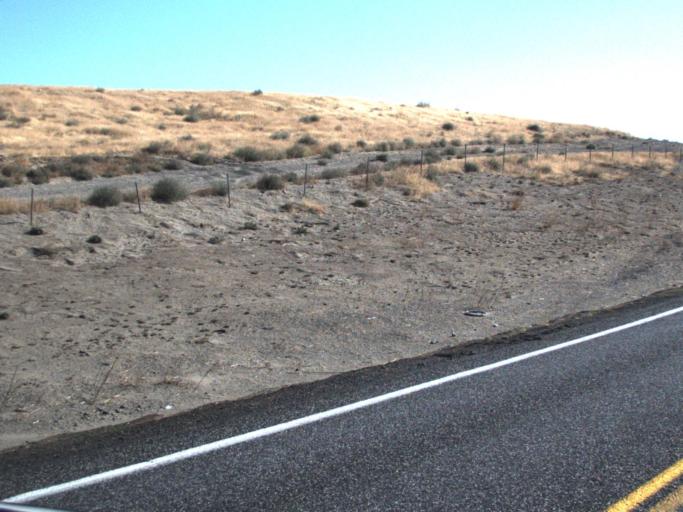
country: US
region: Washington
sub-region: Grant County
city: Desert Aire
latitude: 46.5668
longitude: -119.7224
